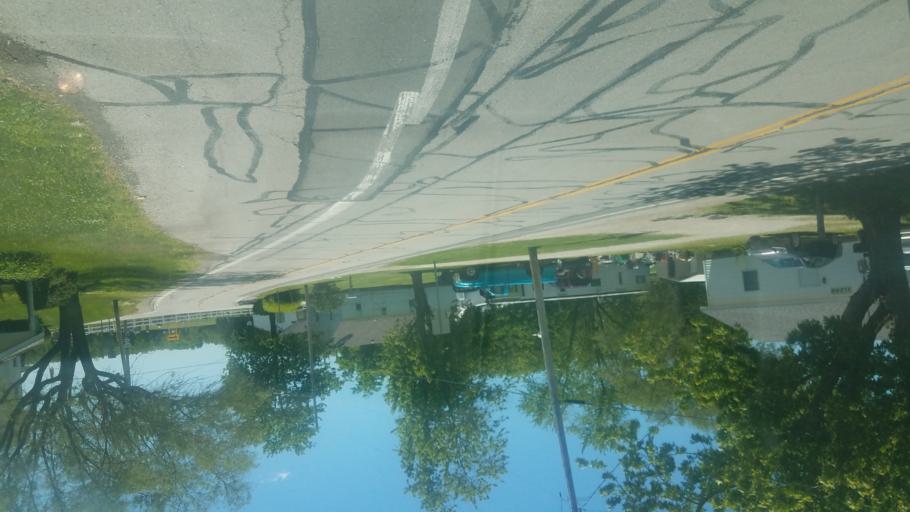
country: US
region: Ohio
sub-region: Darke County
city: Versailles
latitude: 40.2472
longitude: -84.5236
